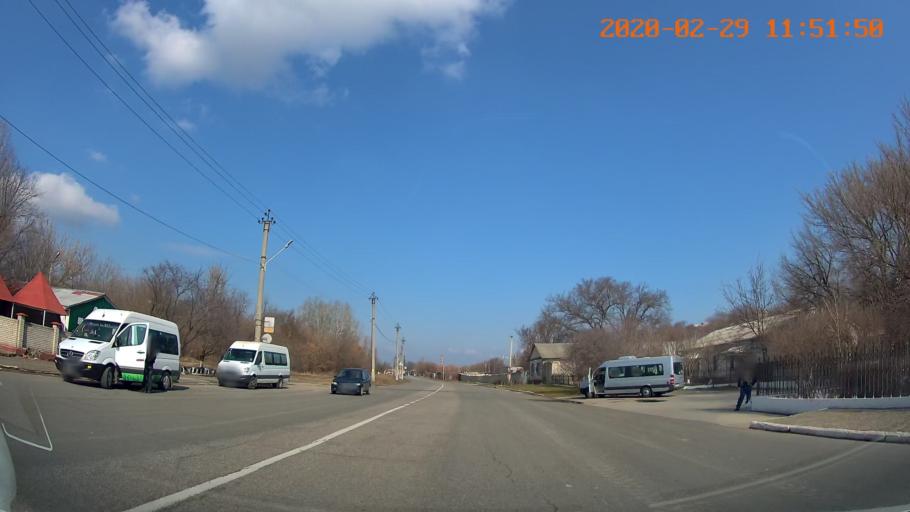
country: MD
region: Telenesti
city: Ribnita
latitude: 47.7670
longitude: 28.9908
